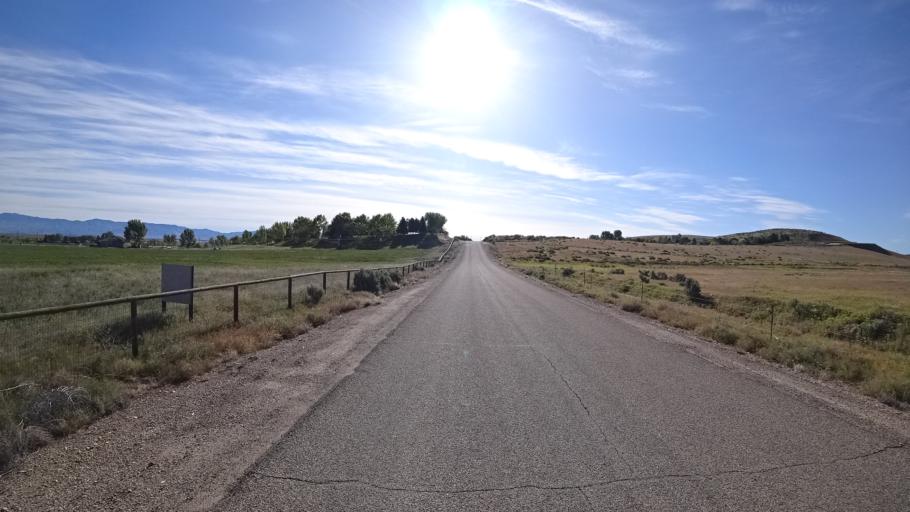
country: US
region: Idaho
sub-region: Ada County
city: Garden City
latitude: 43.5251
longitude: -116.2790
